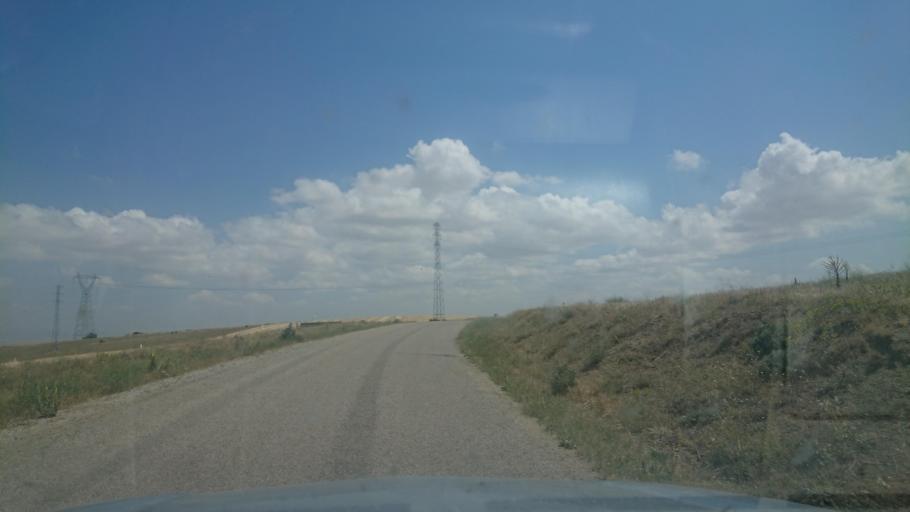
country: TR
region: Aksaray
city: Agacoren
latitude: 38.8685
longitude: 33.9366
